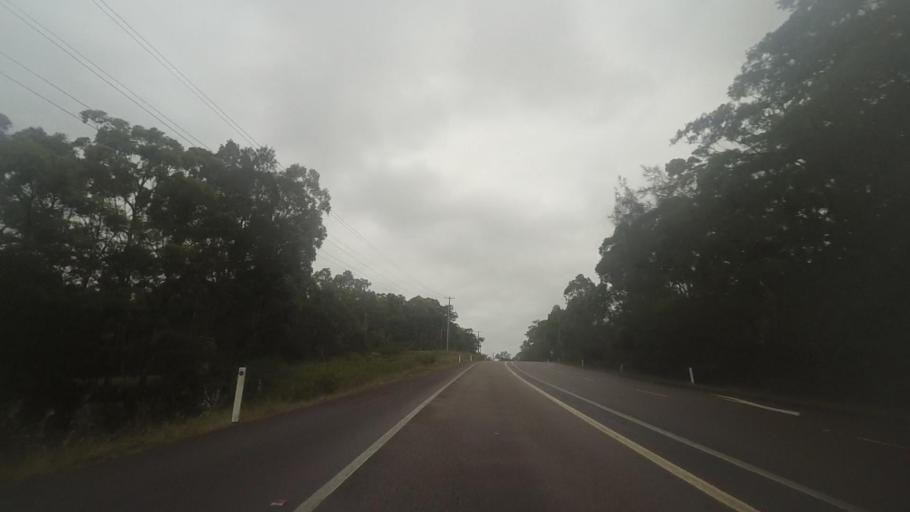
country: AU
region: New South Wales
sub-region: Port Stephens Shire
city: Port Stephens
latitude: -32.6433
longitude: 151.9863
